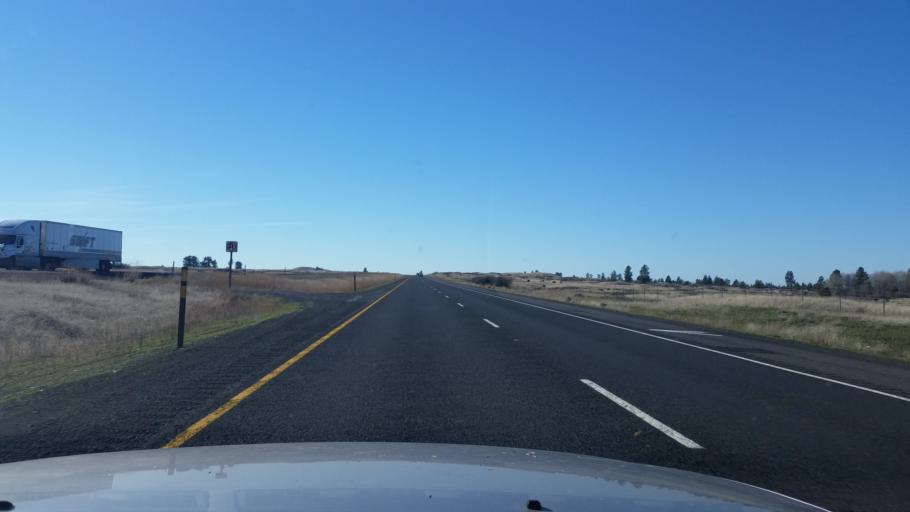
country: US
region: Washington
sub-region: Spokane County
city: Medical Lake
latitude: 47.3911
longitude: -117.8485
